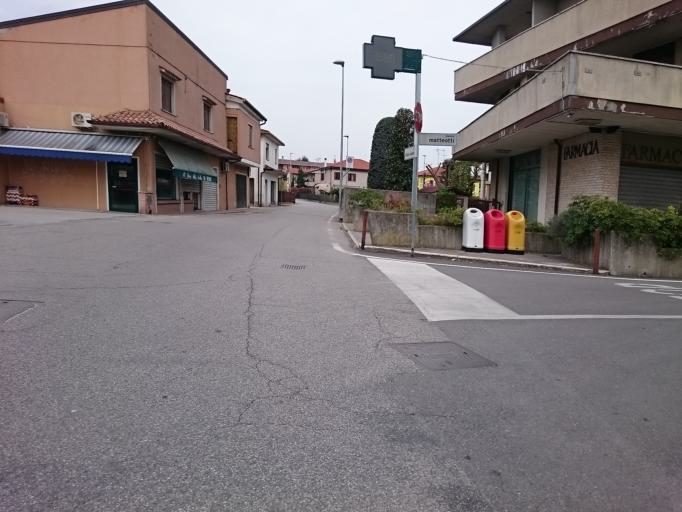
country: IT
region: Veneto
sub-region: Provincia di Padova
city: Anguillara Veneta
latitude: 45.1399
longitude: 11.8868
